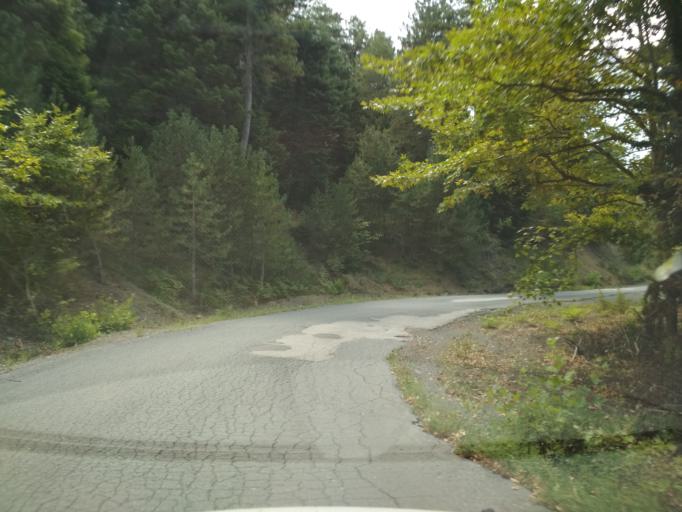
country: GR
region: Central Greece
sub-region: Nomos Evvoias
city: Roviai
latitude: 38.8692
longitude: 23.2931
